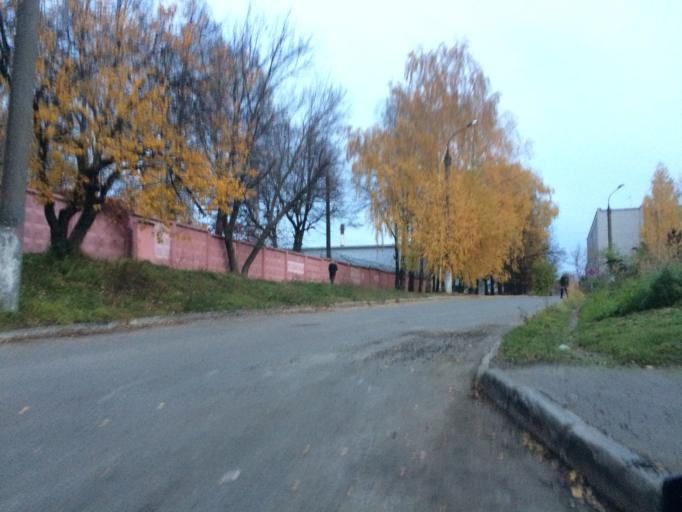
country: RU
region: Mariy-El
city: Yoshkar-Ola
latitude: 56.6189
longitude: 47.8860
